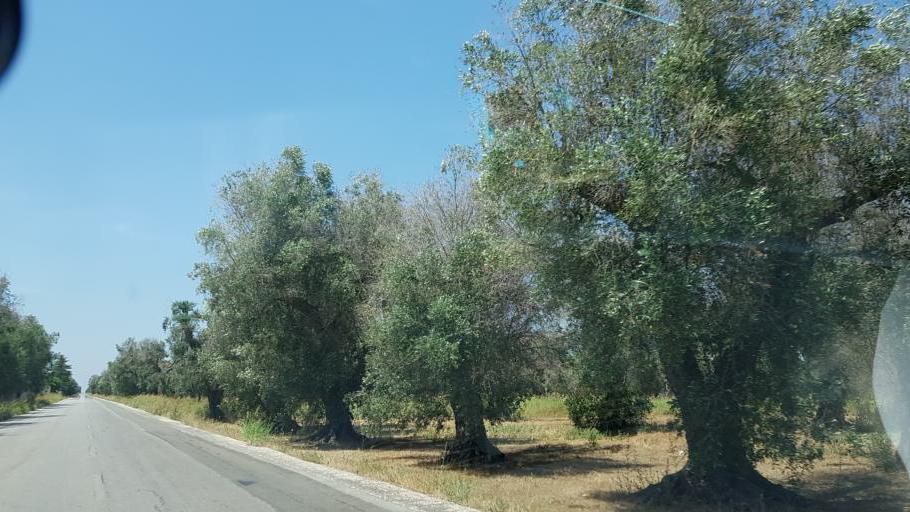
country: IT
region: Apulia
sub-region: Provincia di Brindisi
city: San Donaci
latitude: 40.4708
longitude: 17.8995
